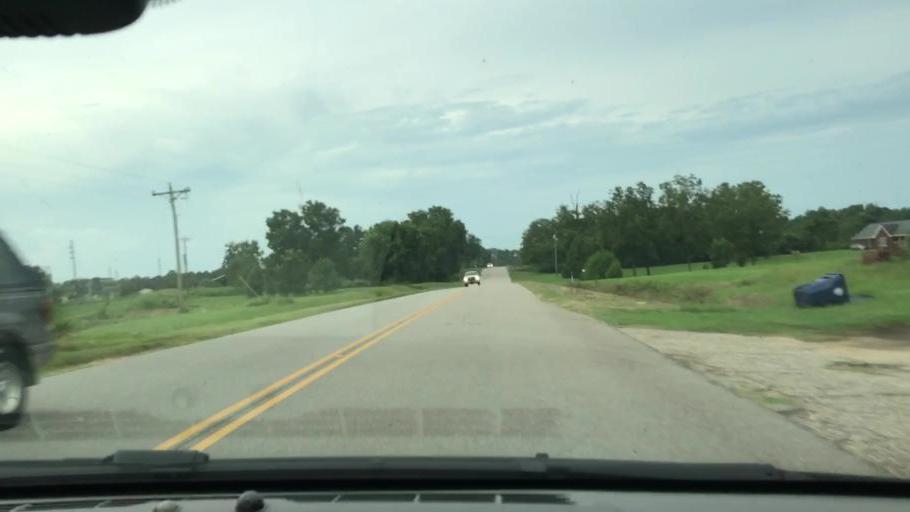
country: US
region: Alabama
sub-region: Houston County
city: Ashford
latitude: 31.2524
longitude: -85.1670
